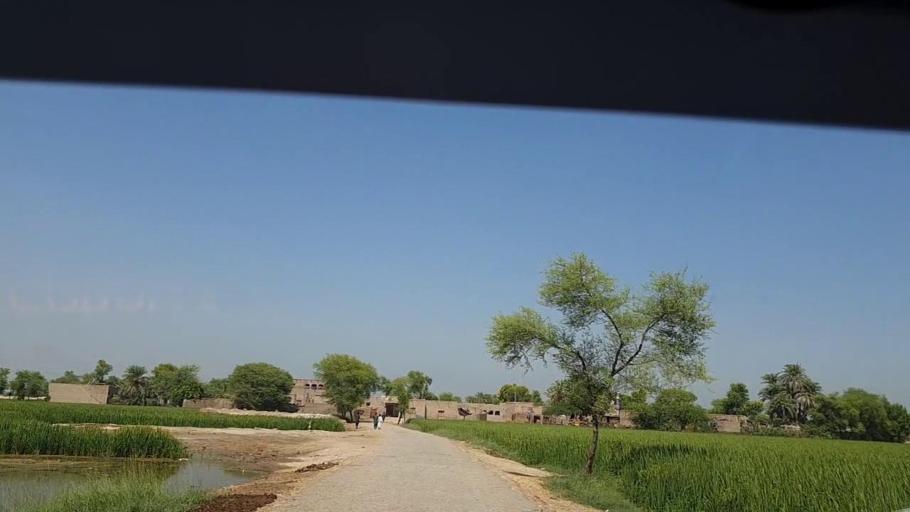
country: PK
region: Sindh
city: Tangwani
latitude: 28.2843
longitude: 69.0379
